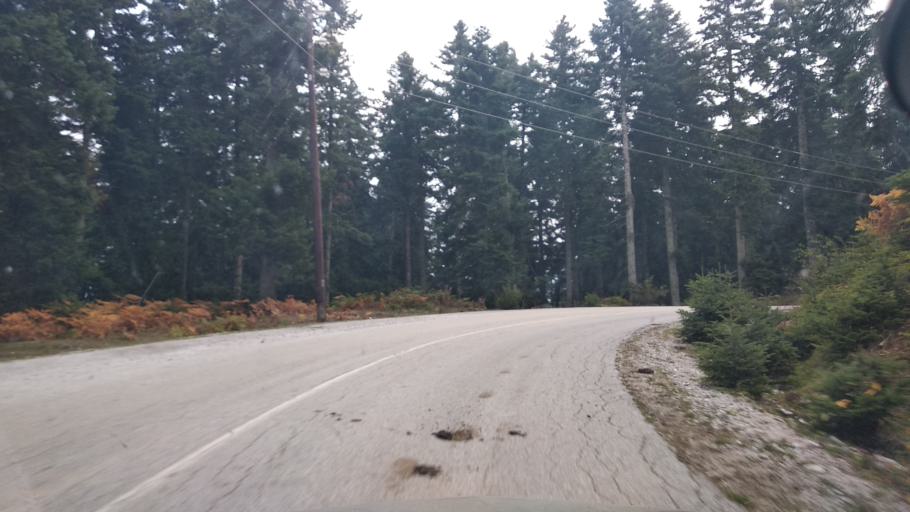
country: GR
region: Thessaly
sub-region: Trikala
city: Pyli
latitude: 39.5764
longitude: 21.4940
